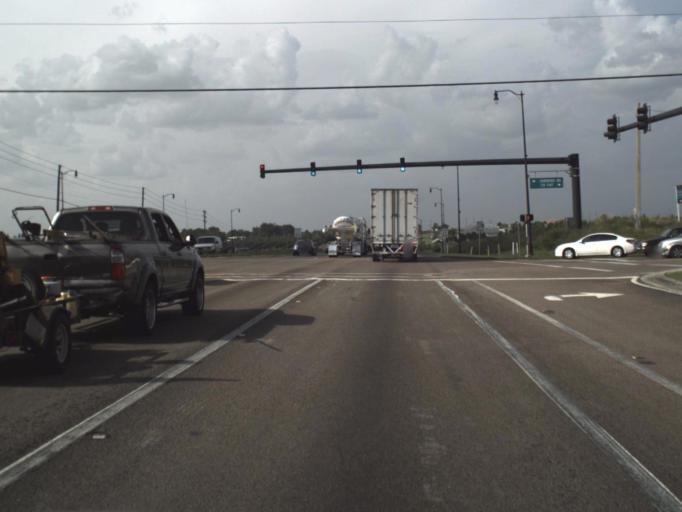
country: US
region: Florida
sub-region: Polk County
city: Davenport
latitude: 28.1573
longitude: -81.6396
